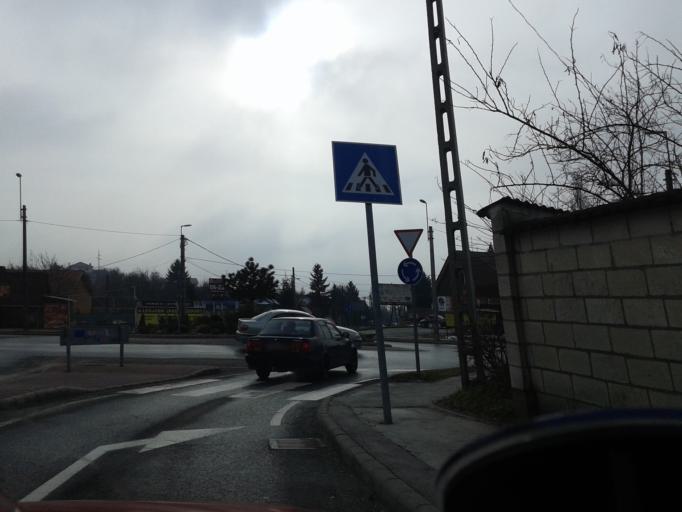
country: HU
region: Pest
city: Diosd
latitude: 47.4074
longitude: 18.9507
